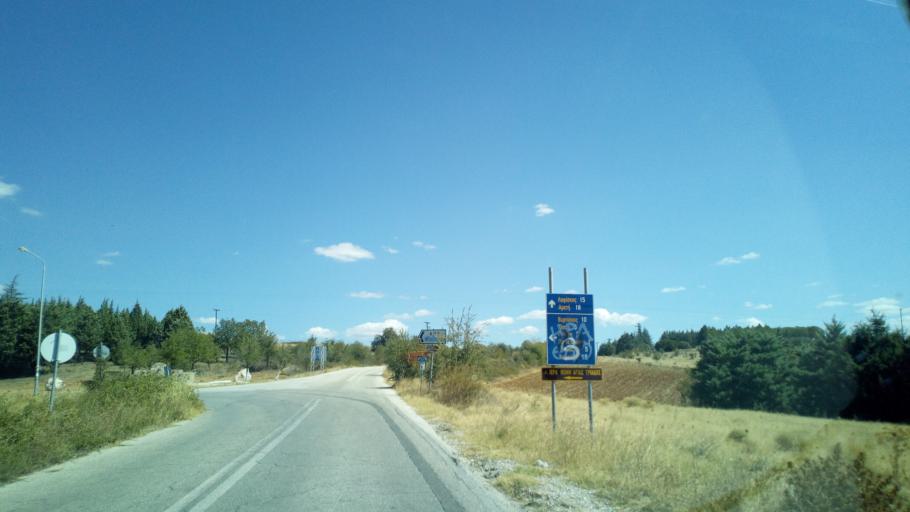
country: GR
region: Central Macedonia
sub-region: Nomos Thessalonikis
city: Kolchikon
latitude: 40.8025
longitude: 23.1513
